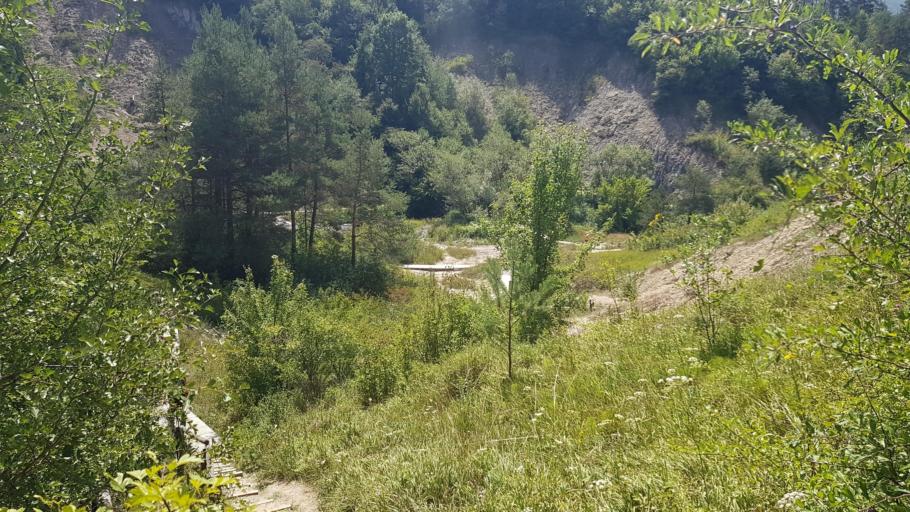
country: RO
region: Harghita
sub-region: Comuna Praid
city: Praid
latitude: 46.5419
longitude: 25.1178
